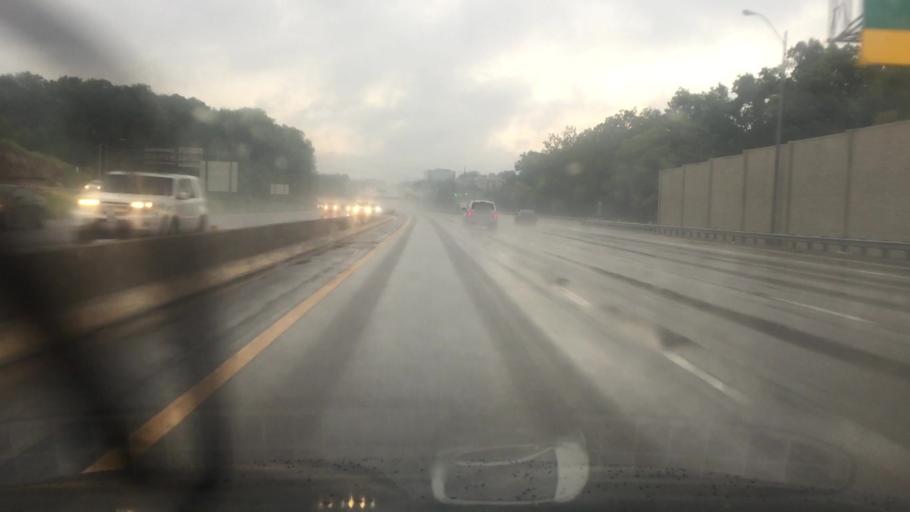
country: US
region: Missouri
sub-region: Saint Louis County
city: Manchester
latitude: 38.6452
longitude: -90.5225
